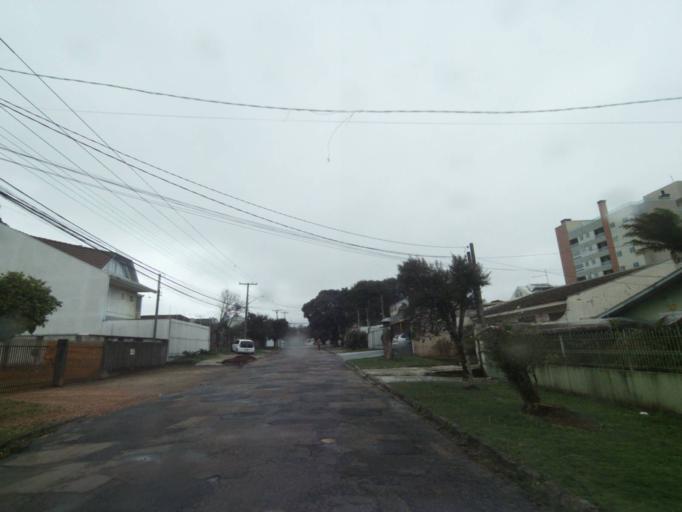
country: BR
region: Parana
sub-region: Curitiba
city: Curitiba
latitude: -25.5094
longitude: -49.3000
